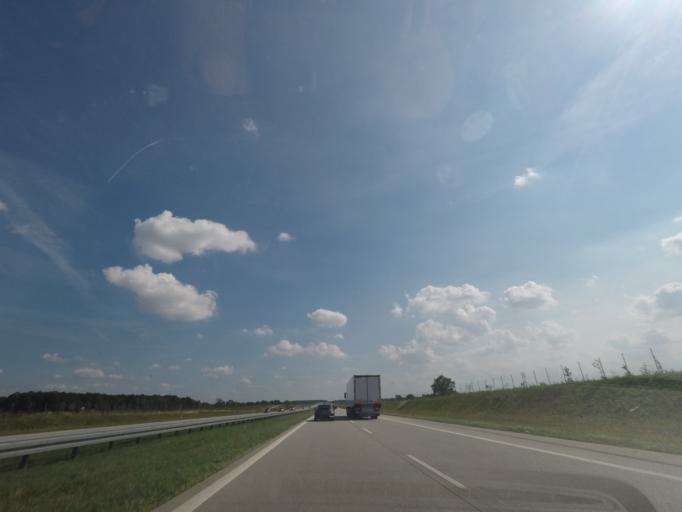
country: PL
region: Lodz Voivodeship
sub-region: Powiat lodzki wschodni
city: Tuszyn
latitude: 51.5885
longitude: 19.5889
